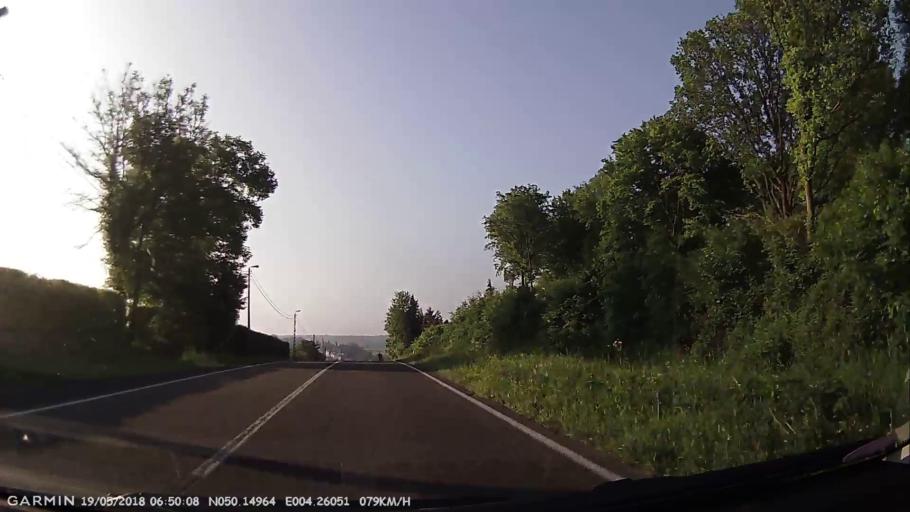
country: BE
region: Wallonia
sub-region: Province du Hainaut
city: Froidchapelle
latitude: 50.1495
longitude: 4.2606
